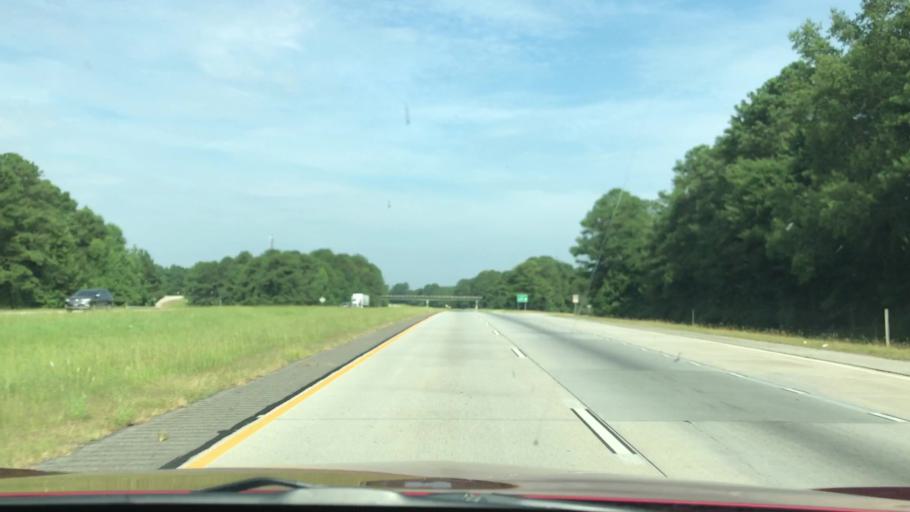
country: US
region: Georgia
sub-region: Warren County
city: Firing Range
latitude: 33.5014
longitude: -82.7080
